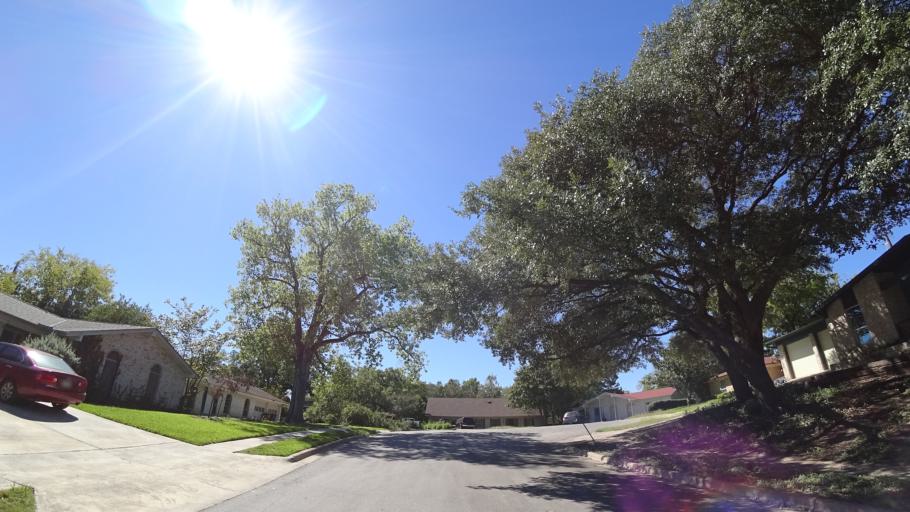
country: US
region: Texas
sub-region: Travis County
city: Austin
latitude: 30.2300
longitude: -97.7397
